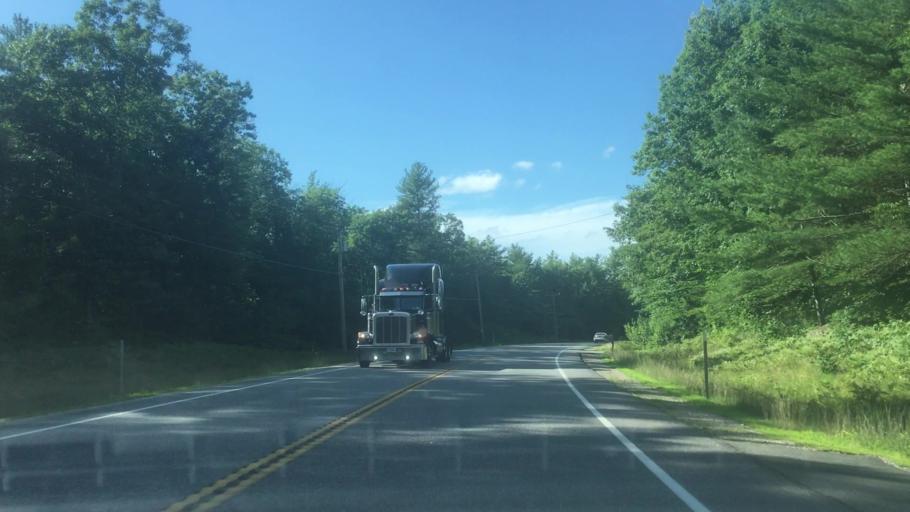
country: US
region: New Hampshire
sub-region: Cheshire County
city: Harrisville
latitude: 43.0470
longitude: -72.0767
